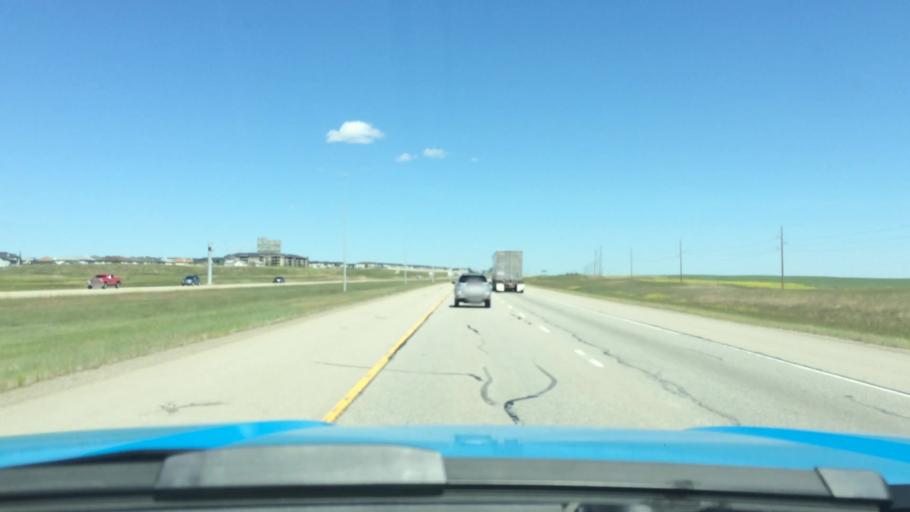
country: CA
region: Alberta
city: Chestermere
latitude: 51.1111
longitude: -113.9201
